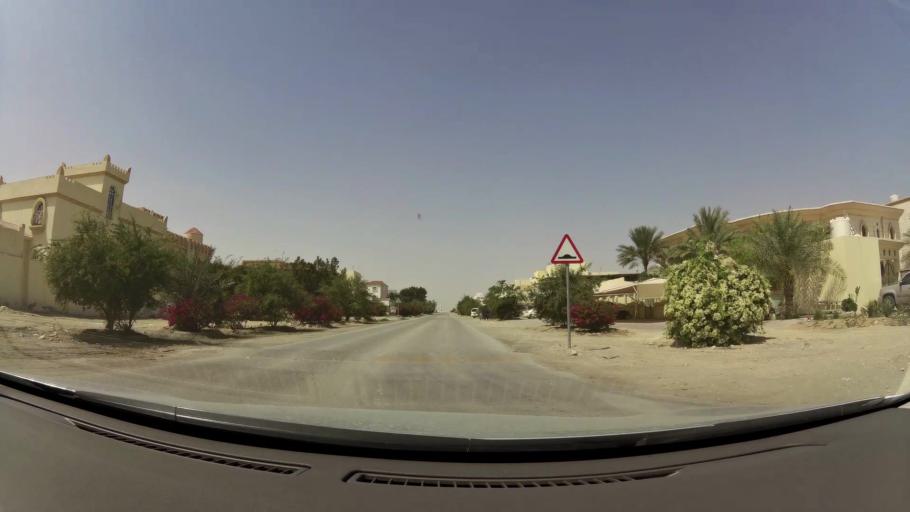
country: QA
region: Baladiyat Umm Salal
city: Umm Salal Muhammad
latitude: 25.3799
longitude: 51.4194
